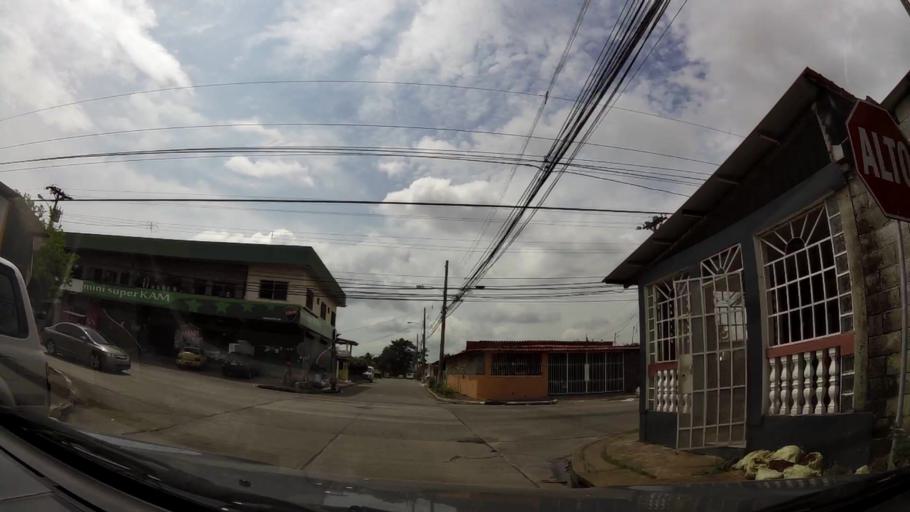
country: PA
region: Panama
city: San Miguelito
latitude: 9.0478
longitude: -79.4188
